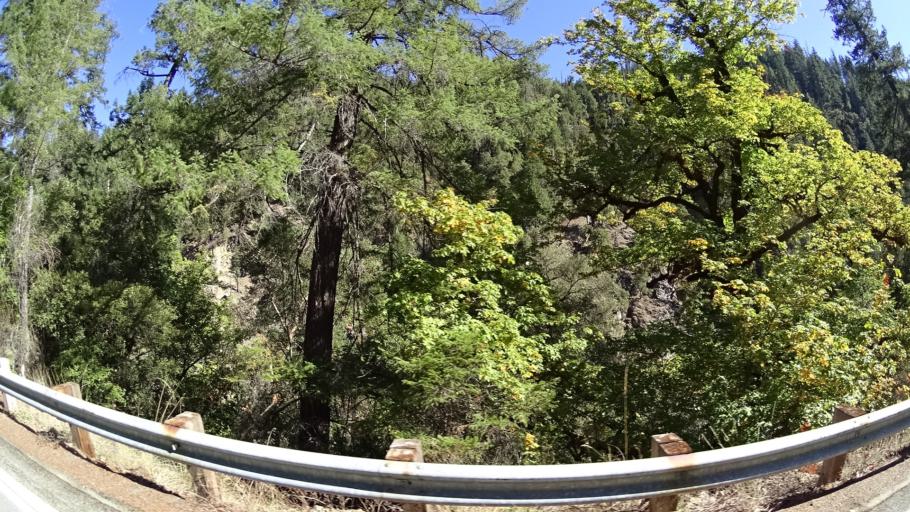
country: US
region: California
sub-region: Siskiyou County
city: Happy Camp
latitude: 41.3560
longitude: -123.4088
